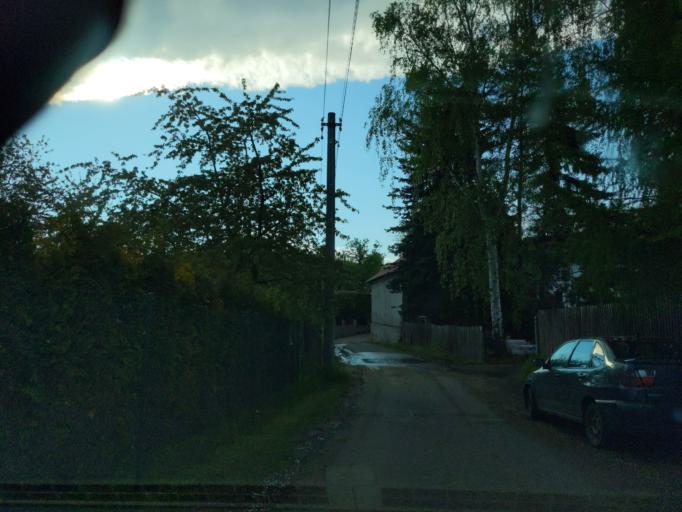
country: CZ
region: Ustecky
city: Libouchec
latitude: 50.7128
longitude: 14.0001
